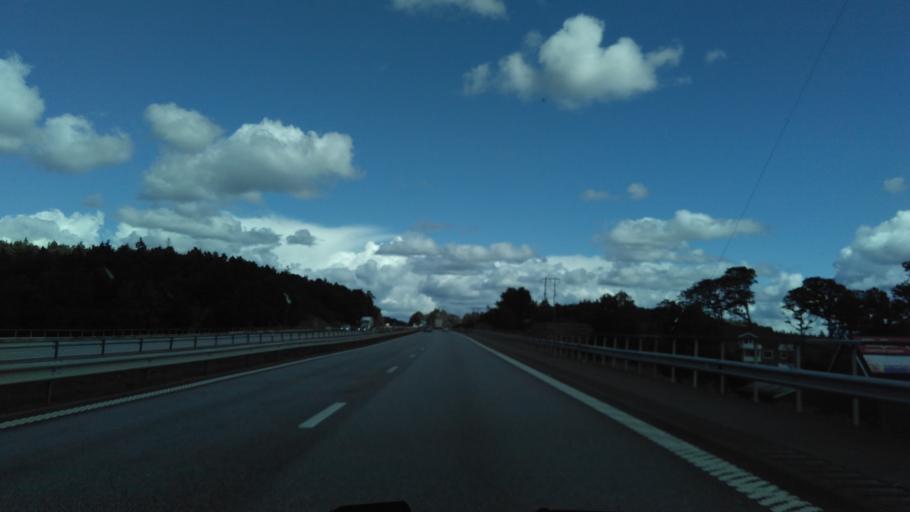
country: SE
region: Vaestra Goetaland
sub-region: Harryda Kommun
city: Molnlycke
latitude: 57.6719
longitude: 12.1188
